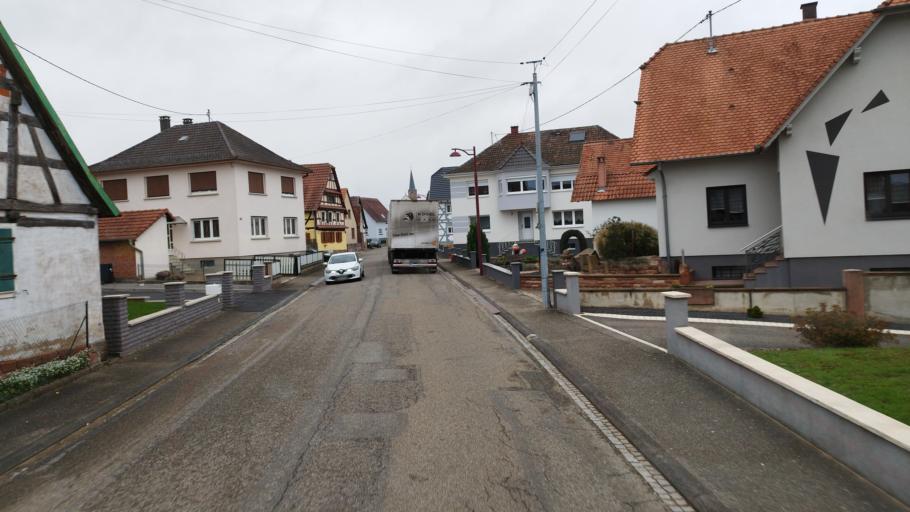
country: DE
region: Rheinland-Pfalz
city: Steinfeld
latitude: 48.9866
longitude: 8.0509
